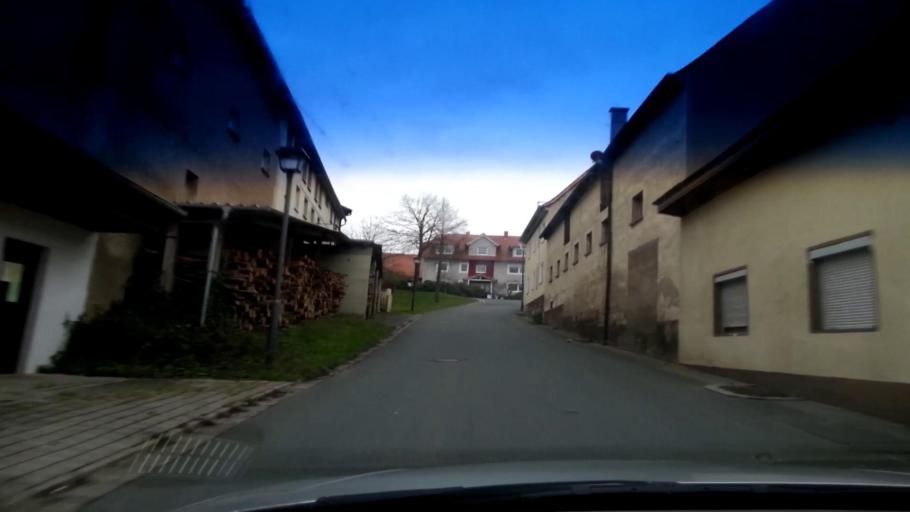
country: DE
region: Bavaria
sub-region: Upper Franconia
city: Pommersfelden
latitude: 49.8186
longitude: 10.8070
